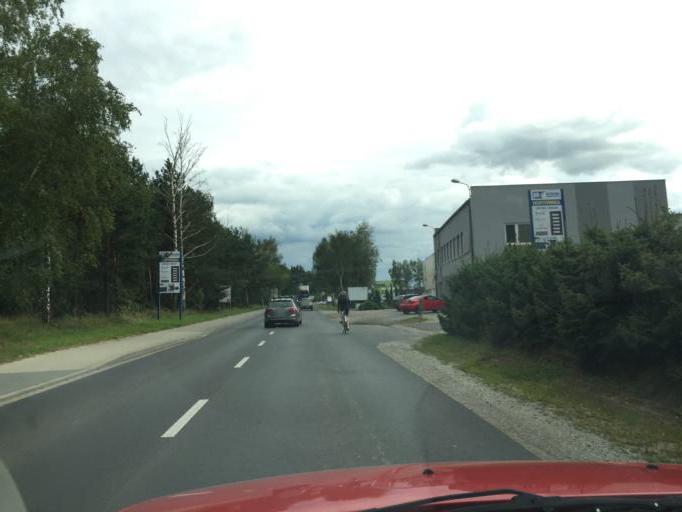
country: PL
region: Greater Poland Voivodeship
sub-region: Powiat poznanski
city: Baranowo
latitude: 52.4073
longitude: 16.7941
